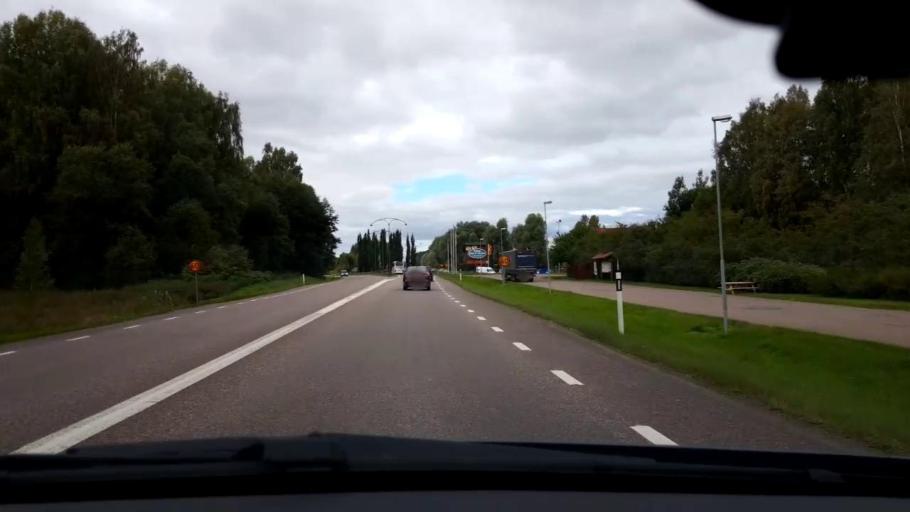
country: SE
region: Dalarna
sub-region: Borlange Kommun
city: Borlaenge
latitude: 60.4719
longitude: 15.4601
